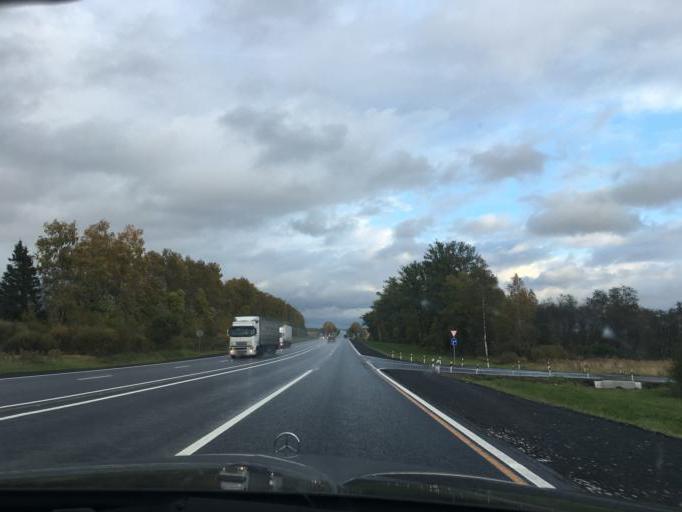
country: RU
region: Smolensk
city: Katyn'
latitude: 54.8486
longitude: 31.7883
